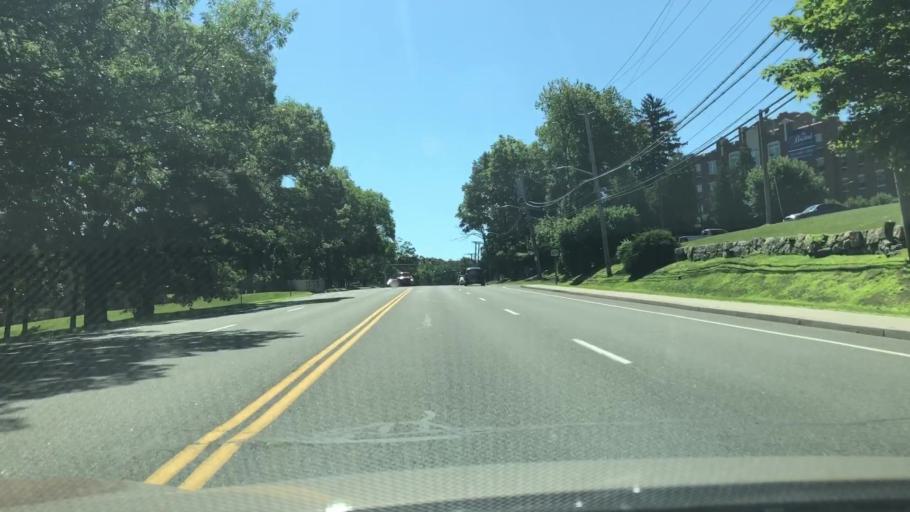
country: US
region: New York
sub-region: Westchester County
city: White Plains
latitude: 41.0282
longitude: -73.7487
